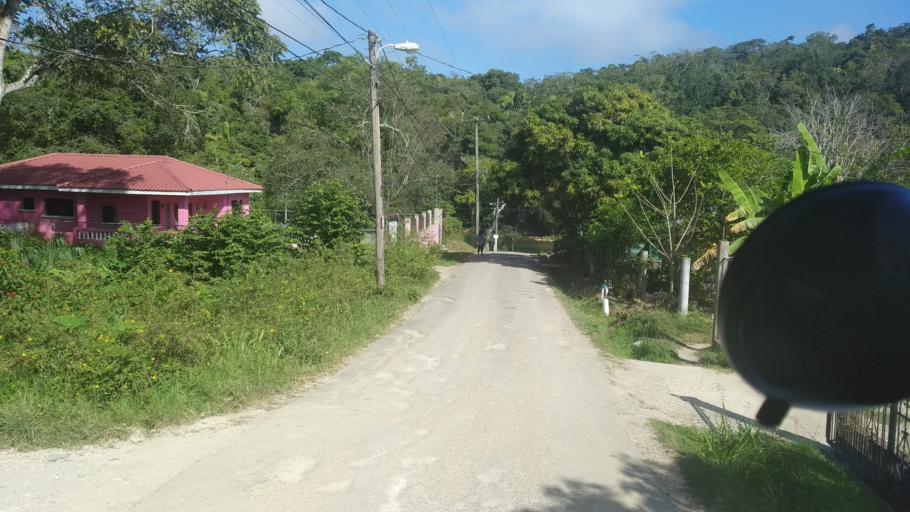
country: BZ
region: Cayo
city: Benque Viejo del Carmen
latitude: 17.0856
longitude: -89.1314
